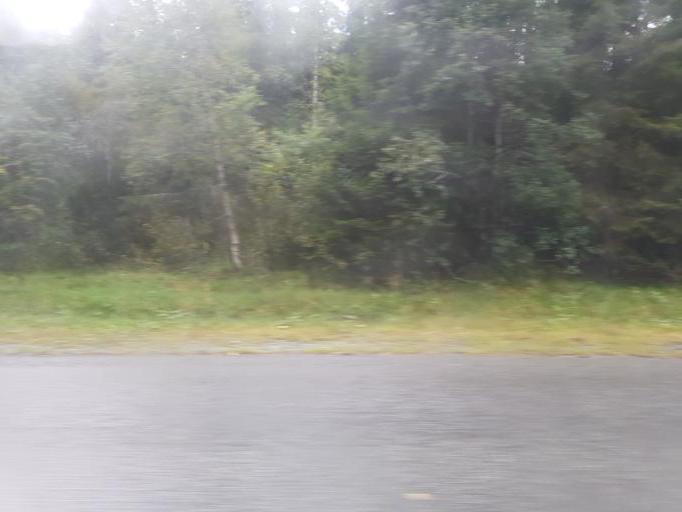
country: NO
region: Sor-Trondelag
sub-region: Trondheim
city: Trondheim
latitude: 63.4156
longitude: 10.3086
